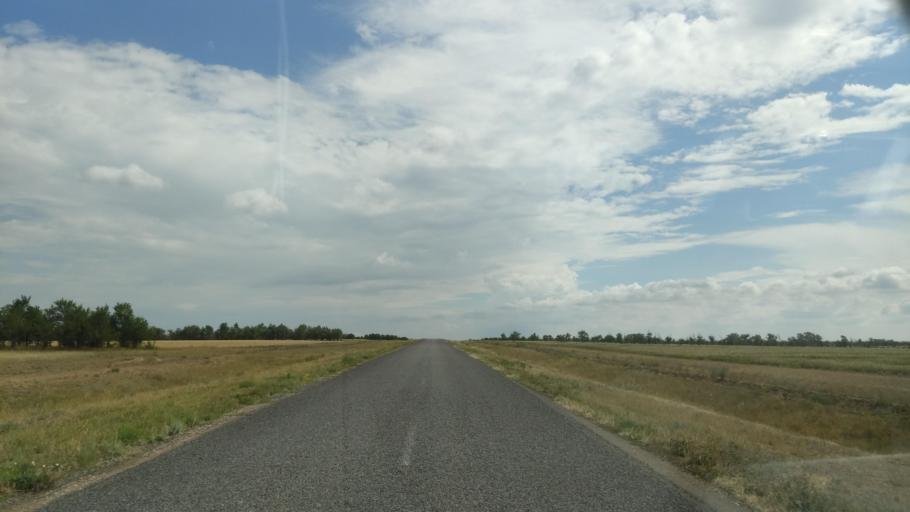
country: KZ
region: Pavlodar
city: Pavlodar
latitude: 52.6366
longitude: 76.9637
